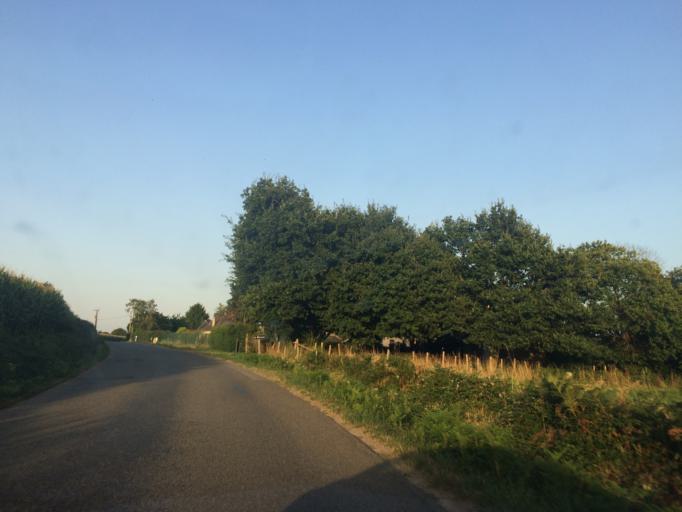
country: FR
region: Brittany
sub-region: Departement du Morbihan
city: Allaire
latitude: 47.6350
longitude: -2.1921
